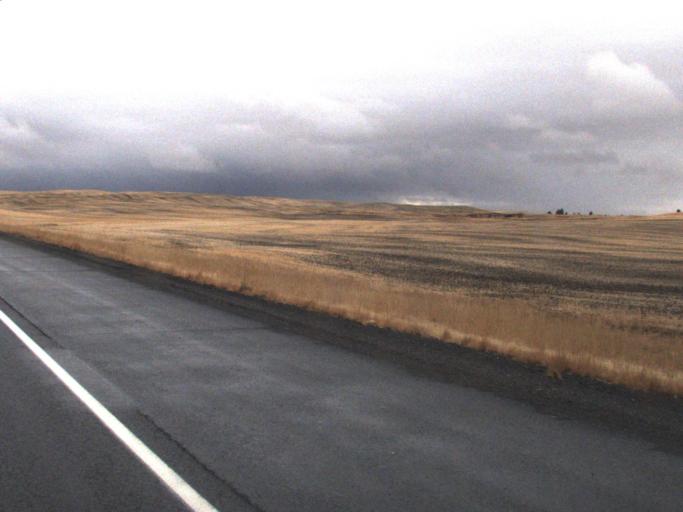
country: US
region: Washington
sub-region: Spokane County
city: Cheney
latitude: 47.4182
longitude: -117.3914
